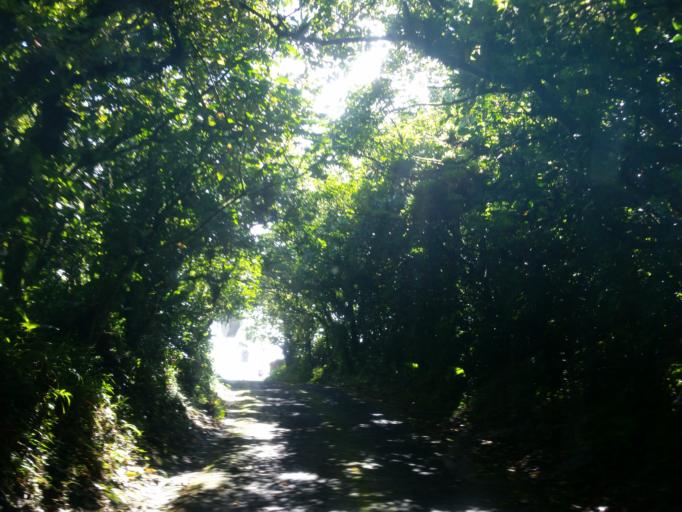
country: NI
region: Granada
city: Diriomo
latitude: 11.8348
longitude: -85.9803
